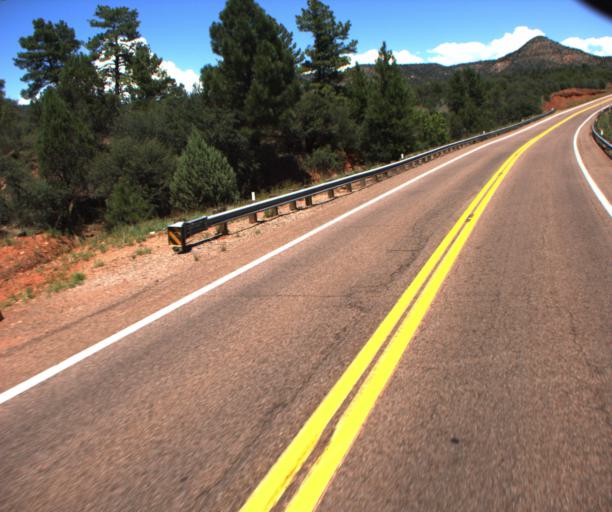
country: US
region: Arizona
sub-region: Navajo County
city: Cibecue
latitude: 33.9535
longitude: -110.3320
